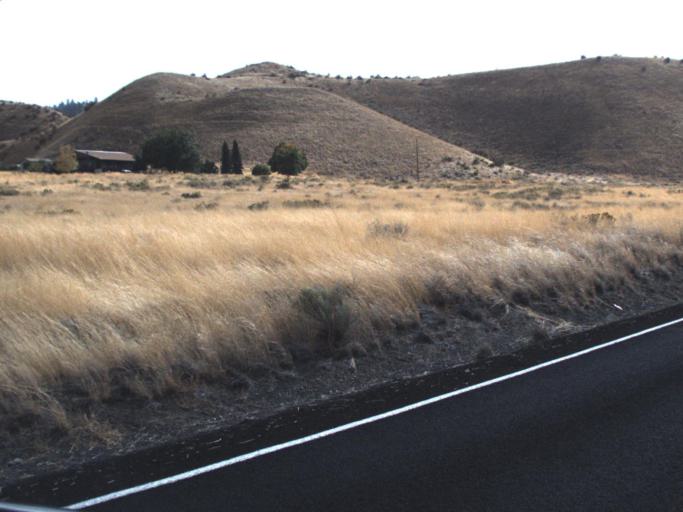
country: US
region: Washington
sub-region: Okanogan County
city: Coulee Dam
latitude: 47.9229
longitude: -118.6896
